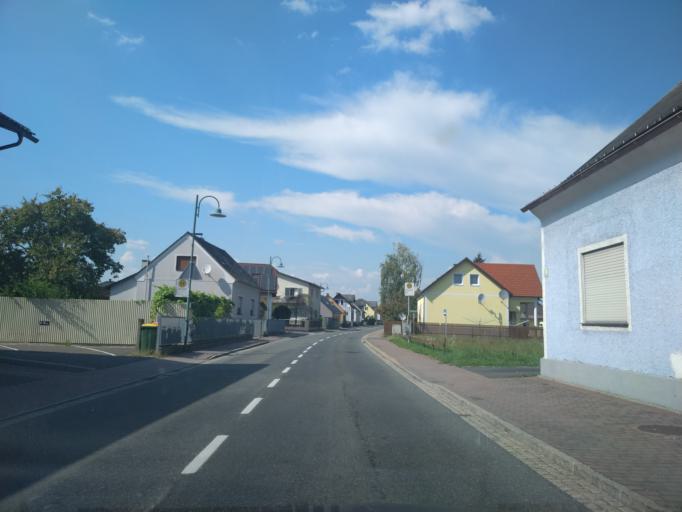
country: AT
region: Styria
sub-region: Politischer Bezirk Leibnitz
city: Kaindorf an der Sulm
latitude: 46.7887
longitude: 15.5385
